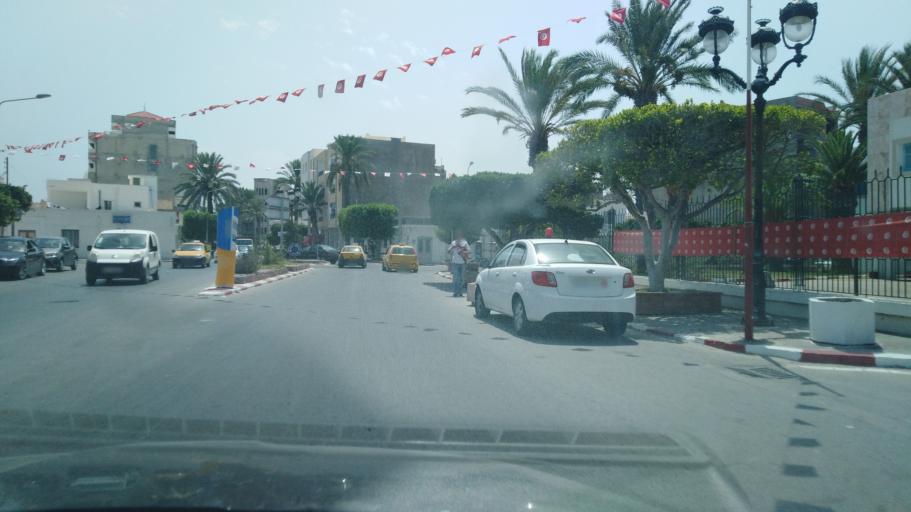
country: TN
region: Al Mahdiyah
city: Mahdia
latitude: 35.5056
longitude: 11.0557
